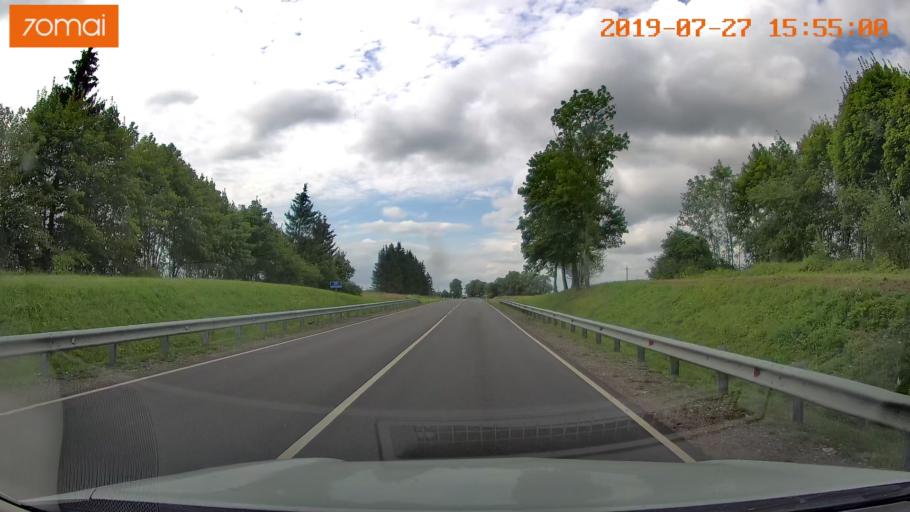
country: RU
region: Kaliningrad
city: Chernyakhovsk
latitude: 54.6110
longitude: 21.9286
